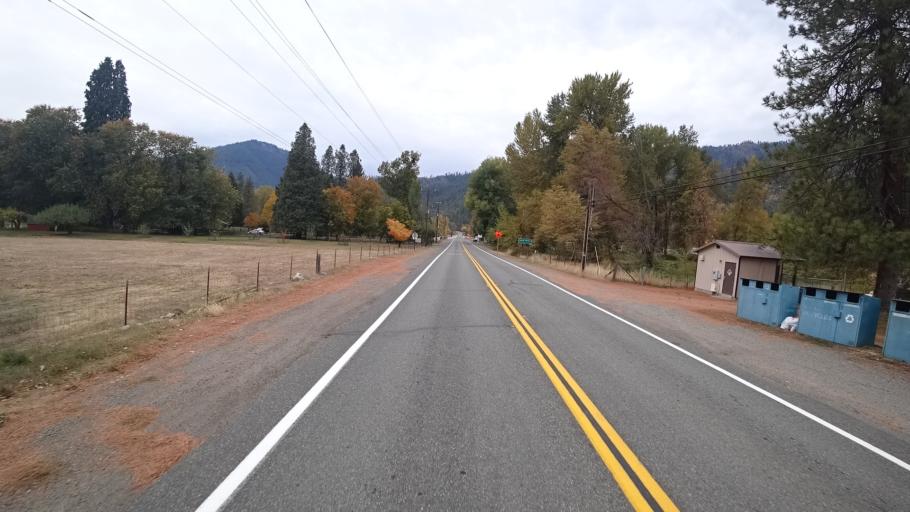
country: US
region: California
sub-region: Siskiyou County
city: Happy Camp
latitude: 41.8413
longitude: -123.1944
